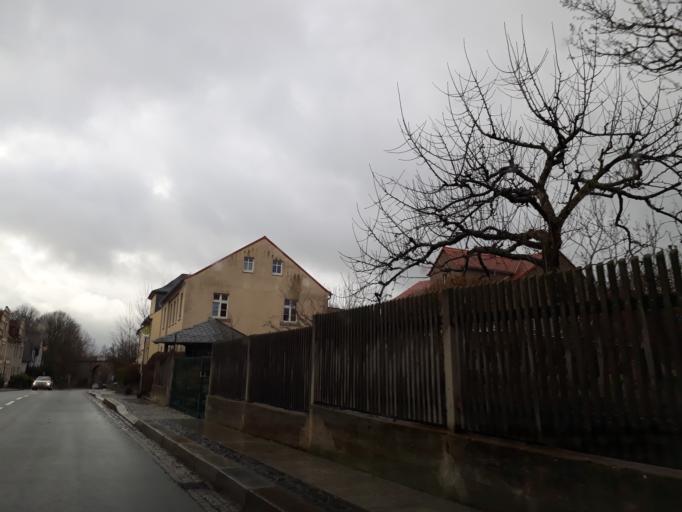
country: DE
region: Saxony
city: Herrnhut
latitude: 51.0176
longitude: 14.7412
